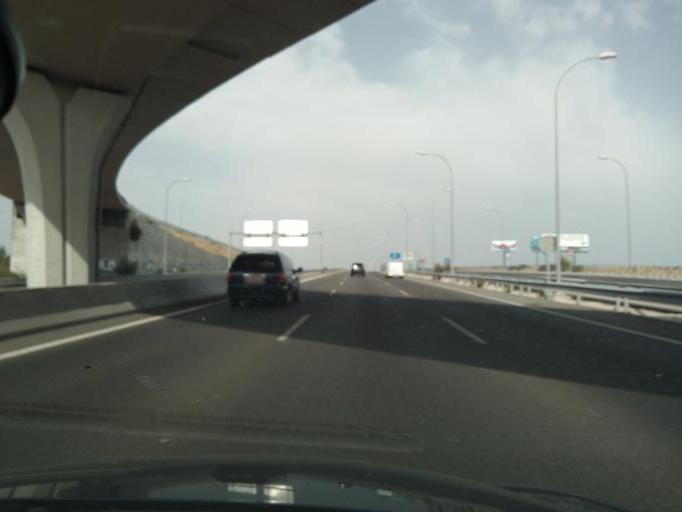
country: ES
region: Madrid
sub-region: Provincia de Madrid
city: Hortaleza
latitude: 40.4722
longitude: -3.6184
